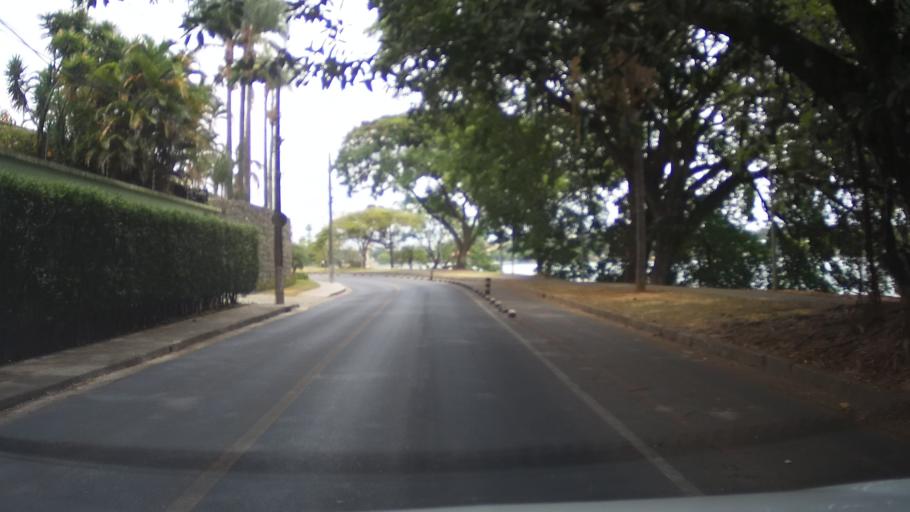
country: BR
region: Minas Gerais
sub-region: Belo Horizonte
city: Belo Horizonte
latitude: -19.8487
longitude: -43.9745
